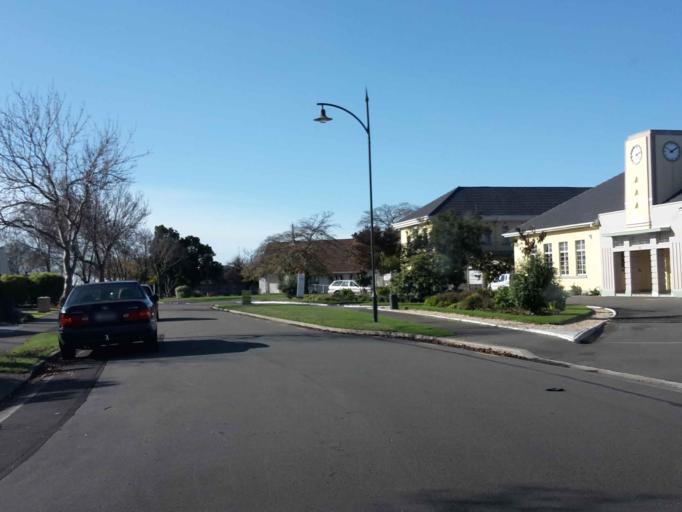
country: NZ
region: Canterbury
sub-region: Selwyn District
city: Prebbleton
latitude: -43.5452
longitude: 172.5453
